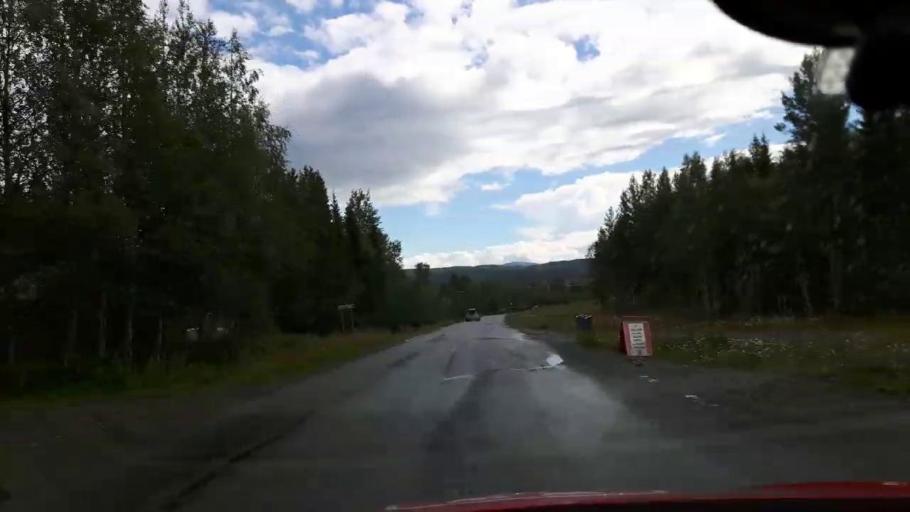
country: SE
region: Jaemtland
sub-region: Are Kommun
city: Are
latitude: 63.3228
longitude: 13.2320
